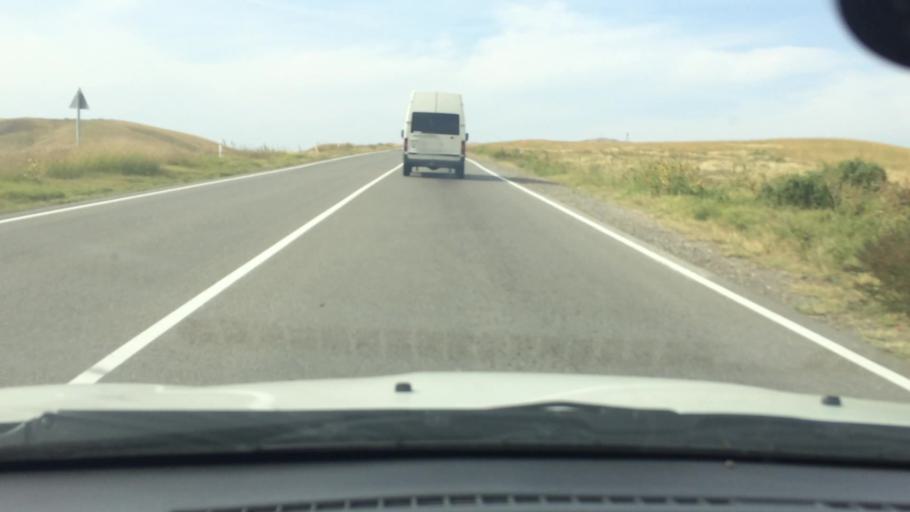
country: GE
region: Kvemo Kartli
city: Rust'avi
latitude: 41.5226
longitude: 44.9851
